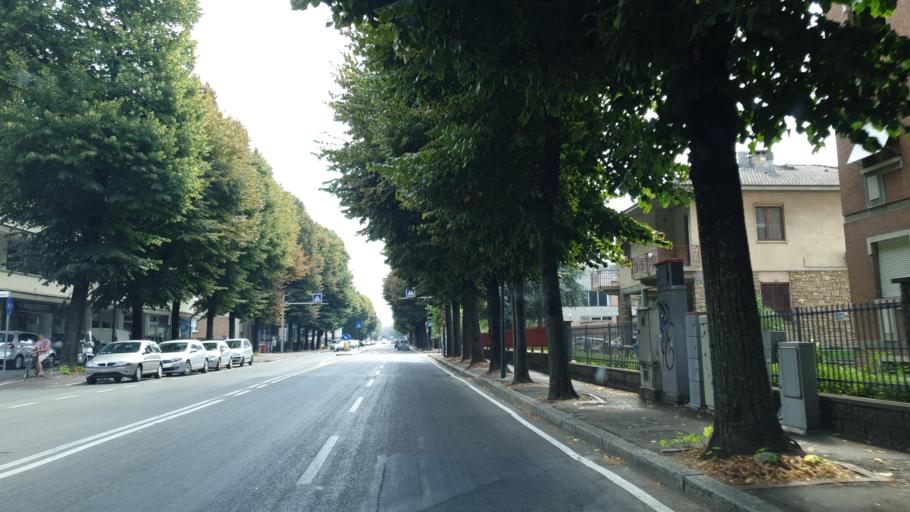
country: IT
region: Emilia-Romagna
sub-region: Provincia di Parma
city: Parma
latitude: 44.8025
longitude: 10.3044
